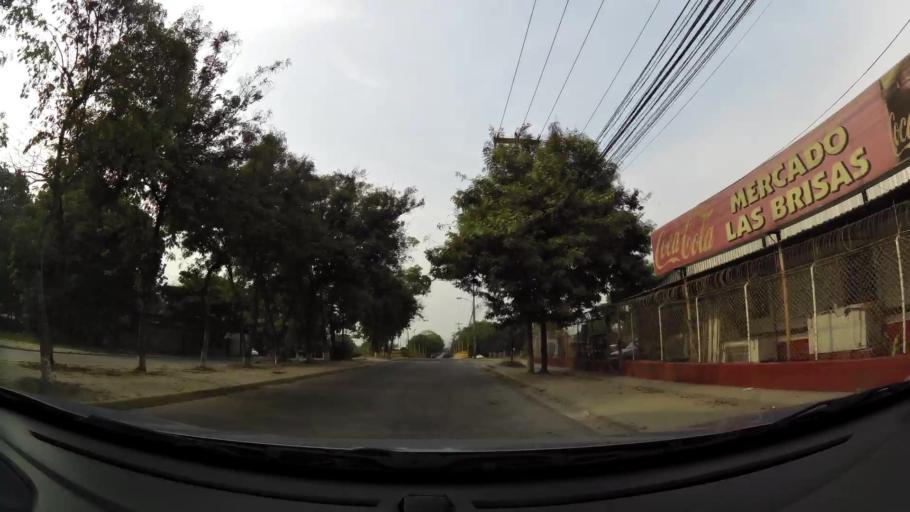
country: HN
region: Cortes
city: San Pedro Sula
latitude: 15.5250
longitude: -88.0157
